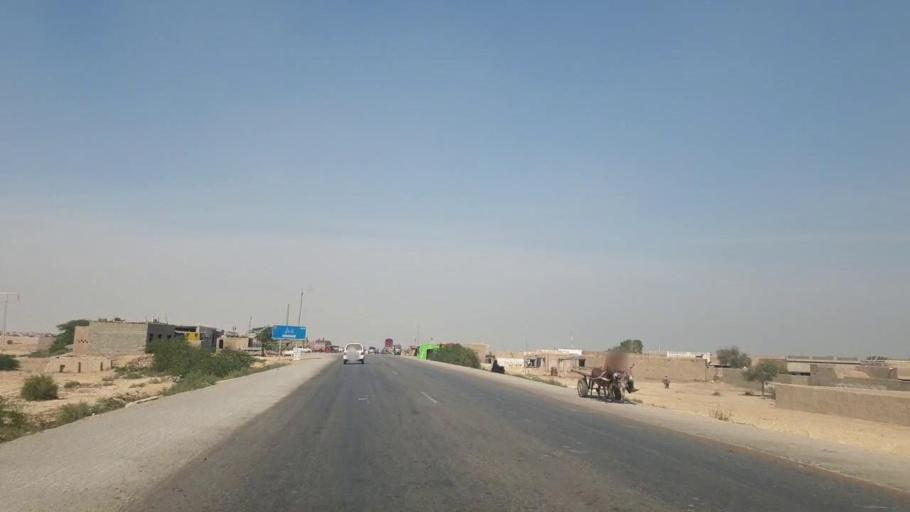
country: PK
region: Sindh
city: Hala
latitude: 25.7917
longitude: 68.2812
